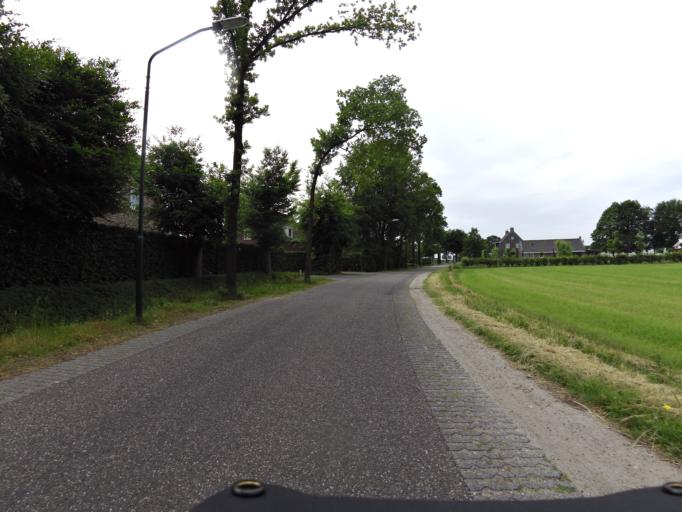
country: NL
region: North Brabant
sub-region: Gemeente Bladel en Netersel
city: Bladel
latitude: 51.3758
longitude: 5.2102
